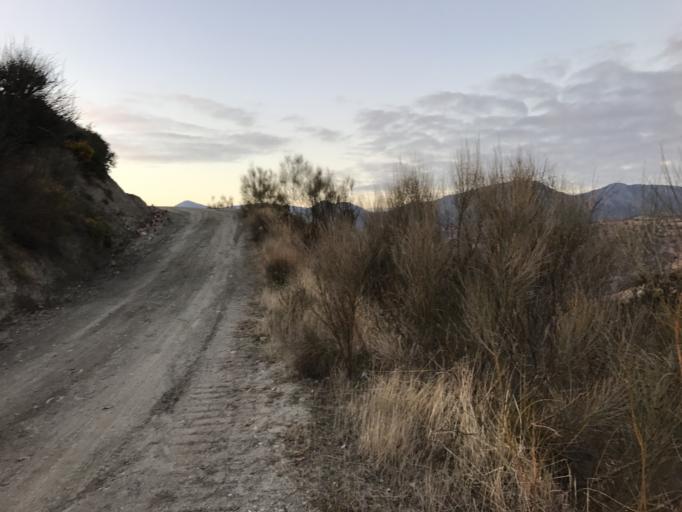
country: ES
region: Andalusia
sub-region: Provincia de Granada
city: Beas de Granada
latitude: 37.2099
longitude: -3.4908
